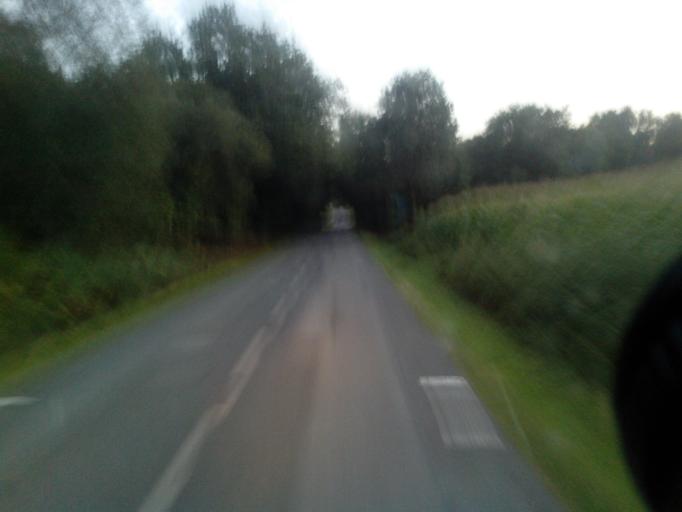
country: FR
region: Brittany
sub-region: Departement d'Ille-et-Vilaine
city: Iffendic
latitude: 48.1041
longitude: -2.0385
